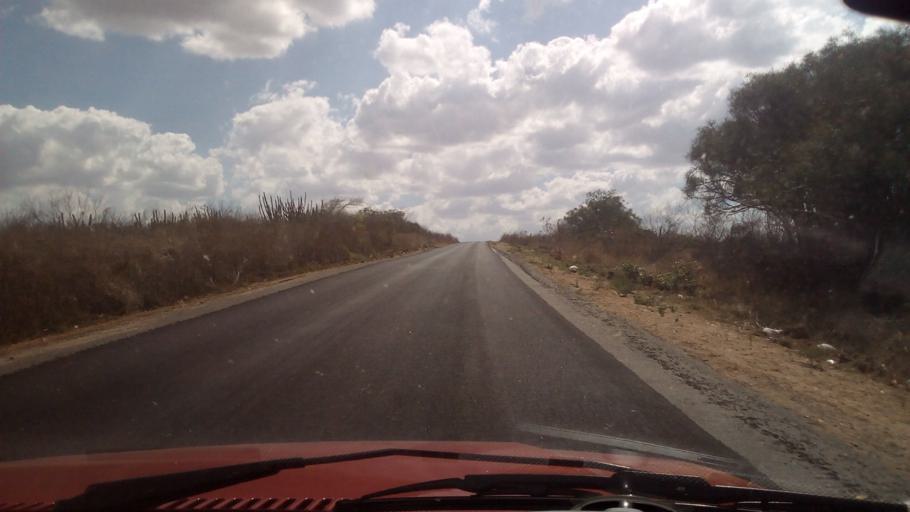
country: BR
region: Paraiba
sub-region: Bananeiras
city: Bananeiras
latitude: -6.7333
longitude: -35.7110
